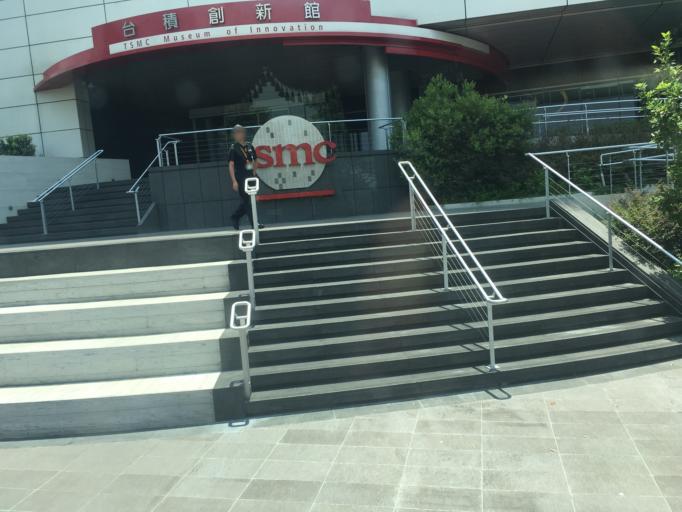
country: TW
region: Taiwan
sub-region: Hsinchu
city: Hsinchu
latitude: 24.7738
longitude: 121.0137
